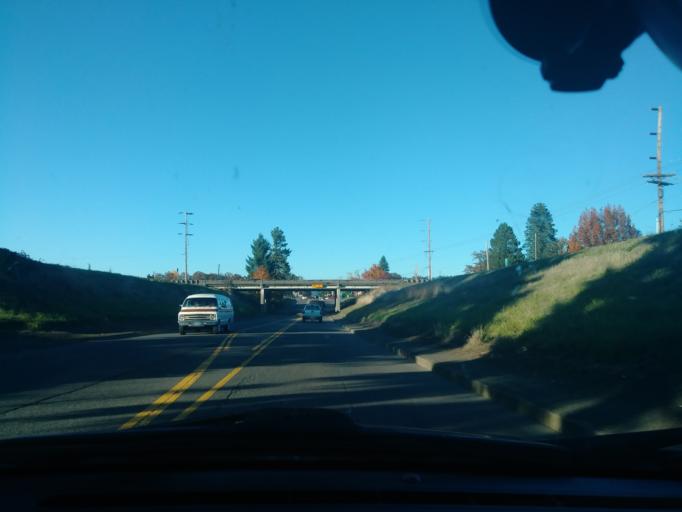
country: US
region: Oregon
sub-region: Washington County
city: Banks
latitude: 45.6082
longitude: -123.1144
